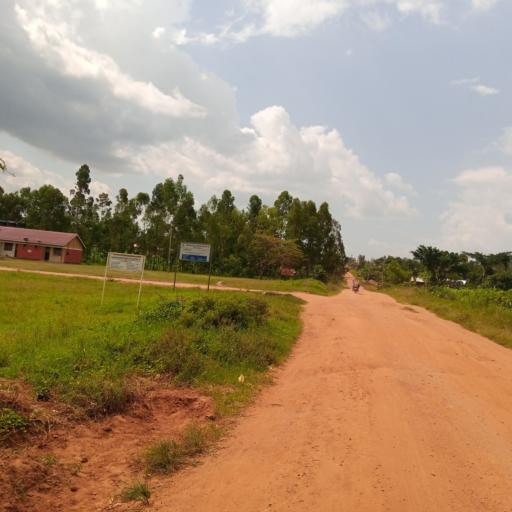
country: UG
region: Eastern Region
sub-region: Mbale District
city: Mbale
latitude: 1.1121
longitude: 34.2021
